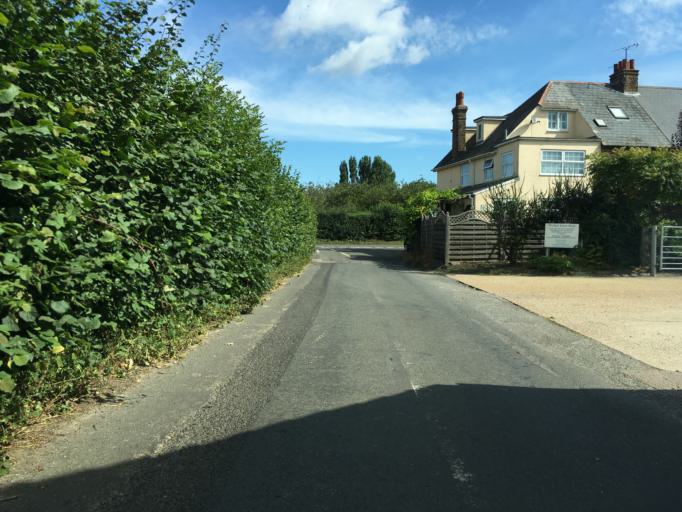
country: GB
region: England
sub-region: Kent
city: Maidstone
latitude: 51.2279
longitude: 0.5517
